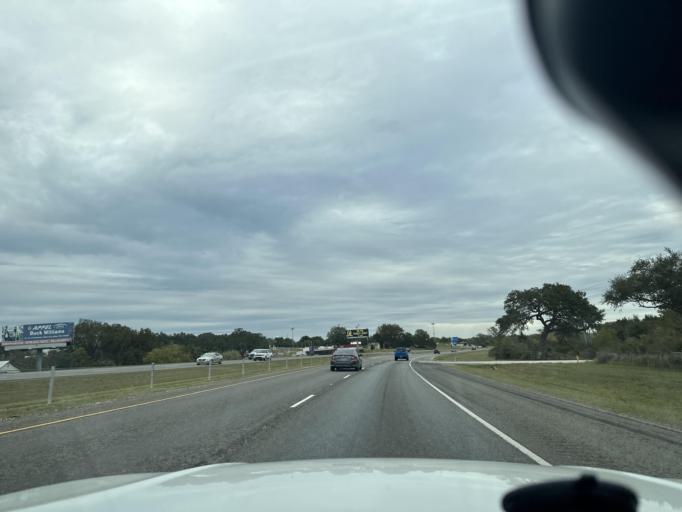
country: US
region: Texas
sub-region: Burleson County
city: Somerville
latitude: 30.1734
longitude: -96.6043
